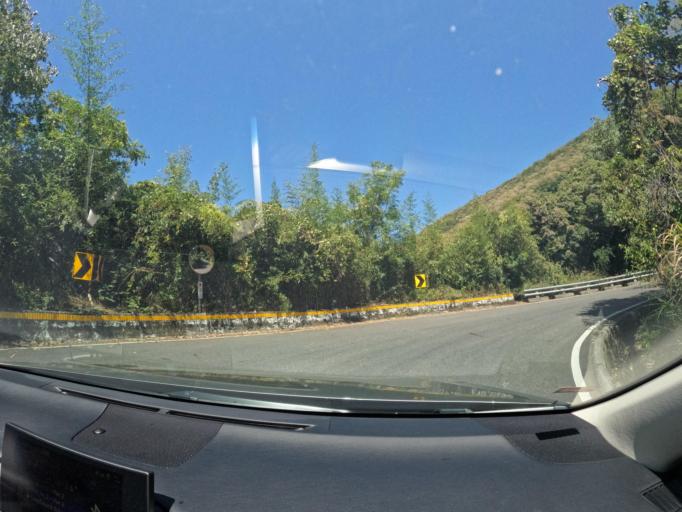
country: TW
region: Taiwan
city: Yujing
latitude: 23.2671
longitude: 120.8478
